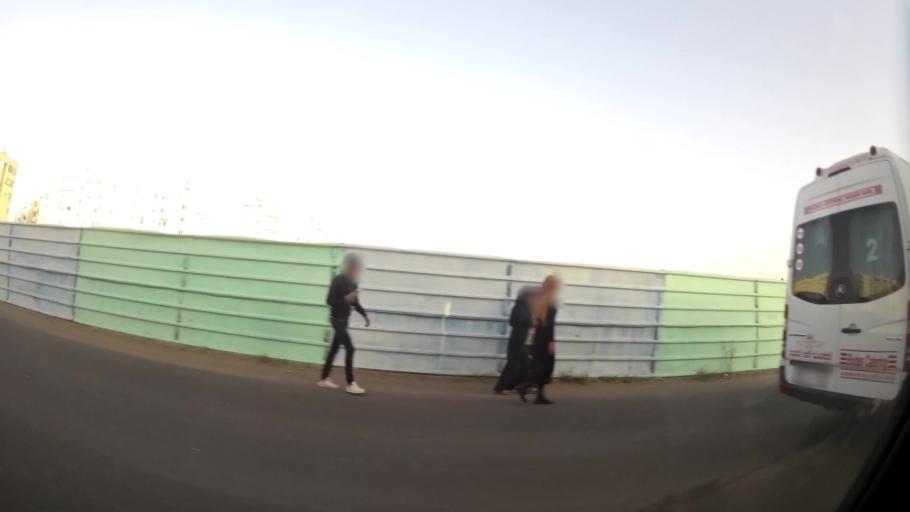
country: MA
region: Oued ed Dahab-Lagouira
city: Dakhla
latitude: 30.3981
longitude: -9.5569
